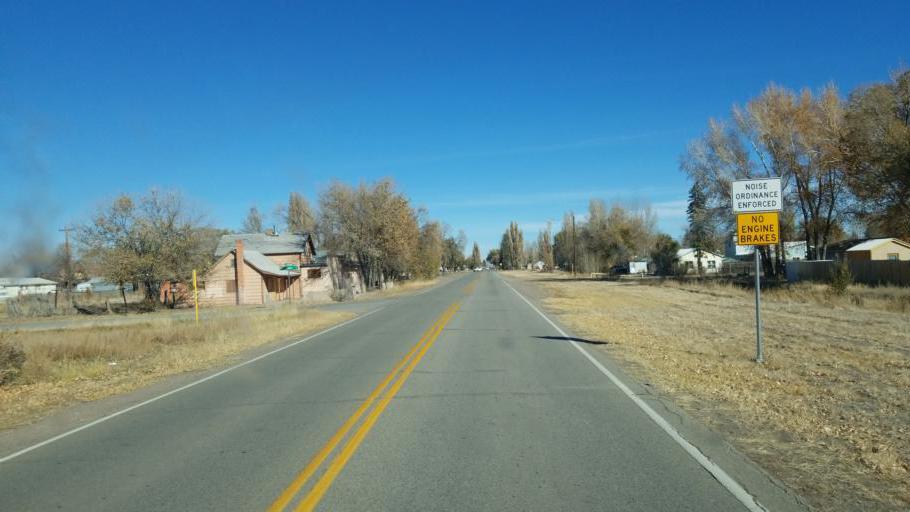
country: US
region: Colorado
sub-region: Rio Grande County
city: Monte Vista
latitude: 37.5721
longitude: -106.1494
